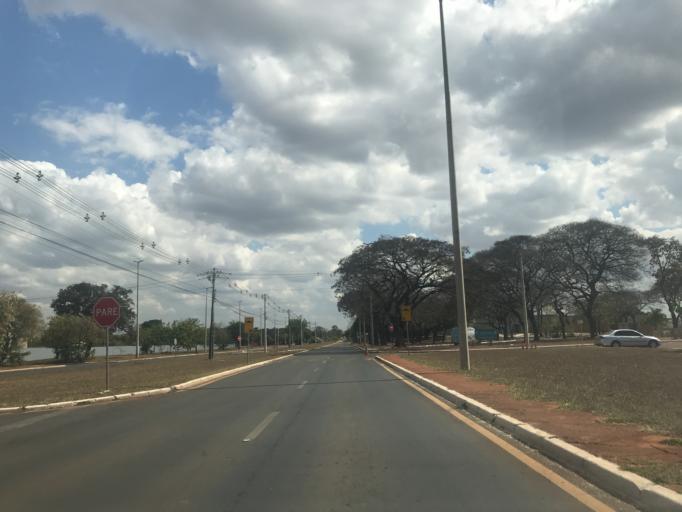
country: BR
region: Federal District
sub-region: Brasilia
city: Brasilia
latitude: -15.8274
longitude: -47.9346
